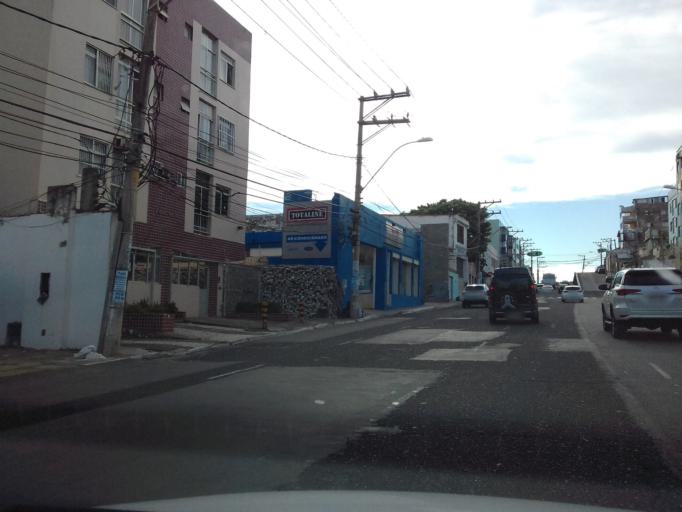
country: BR
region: Bahia
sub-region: Salvador
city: Salvador
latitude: -13.0131
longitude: -38.4751
